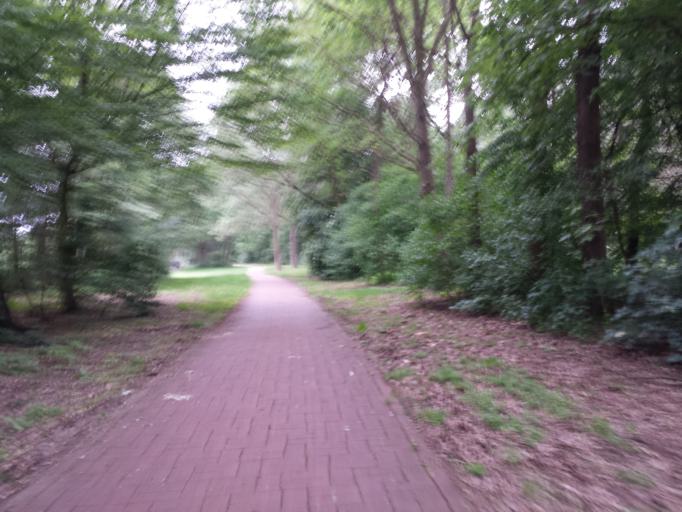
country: DE
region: Bremen
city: Bremen
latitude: 53.1145
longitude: 8.8292
